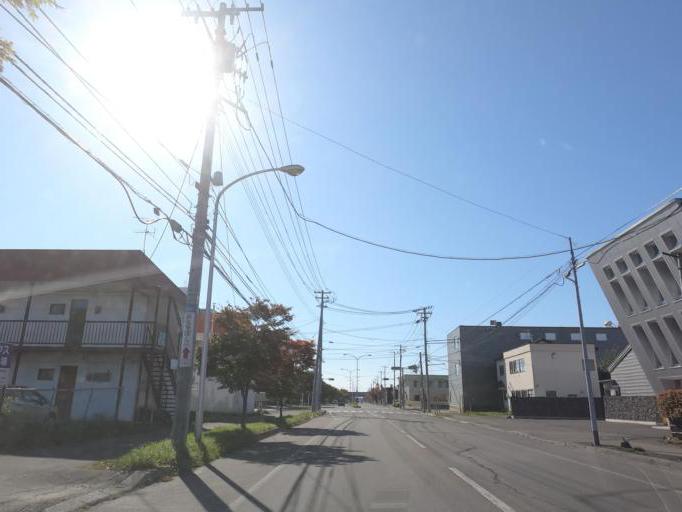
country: JP
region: Hokkaido
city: Obihiro
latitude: 42.9183
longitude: 143.2122
